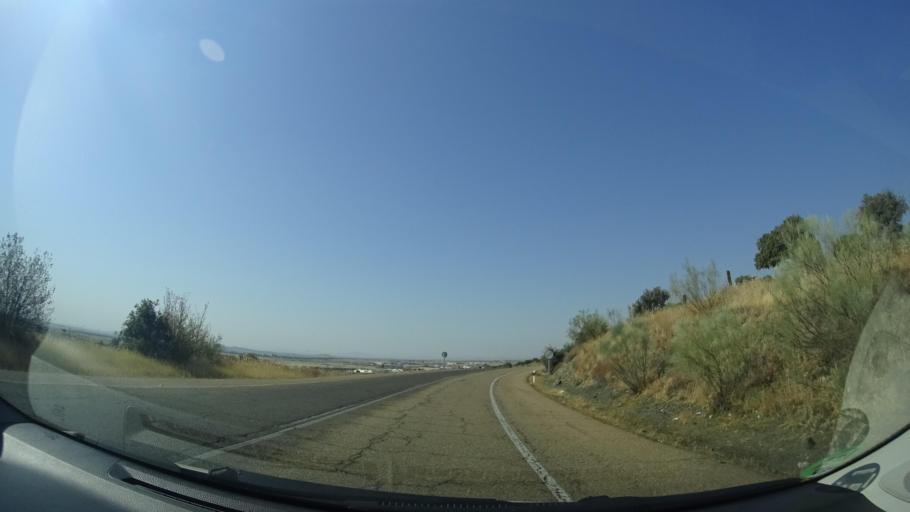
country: ES
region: Extremadura
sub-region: Provincia de Caceres
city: Escurial
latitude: 39.1673
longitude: -5.8981
